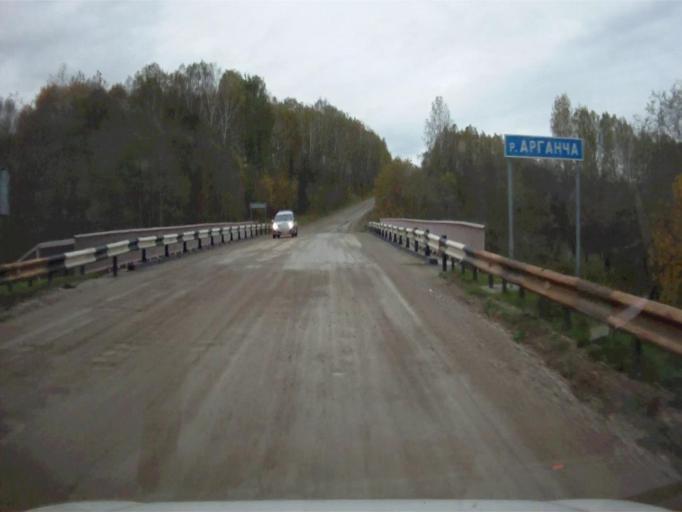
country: RU
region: Chelyabinsk
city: Nyazepetrovsk
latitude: 56.1338
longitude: 59.3122
